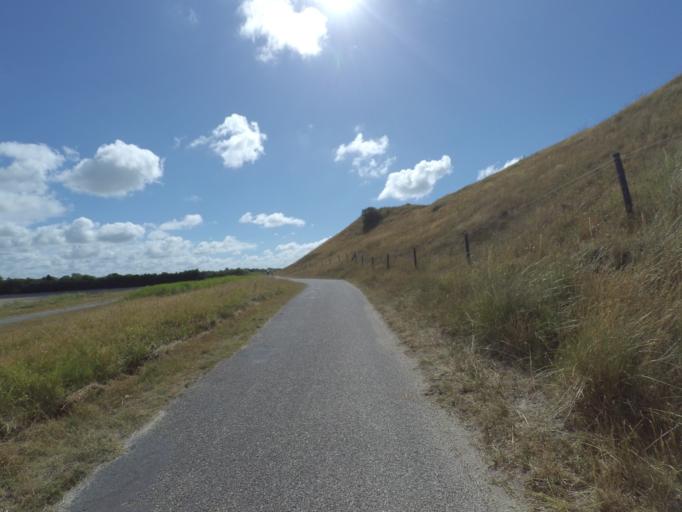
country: NL
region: North Holland
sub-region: Gemeente Texel
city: Den Burg
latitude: 53.1301
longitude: 4.8156
